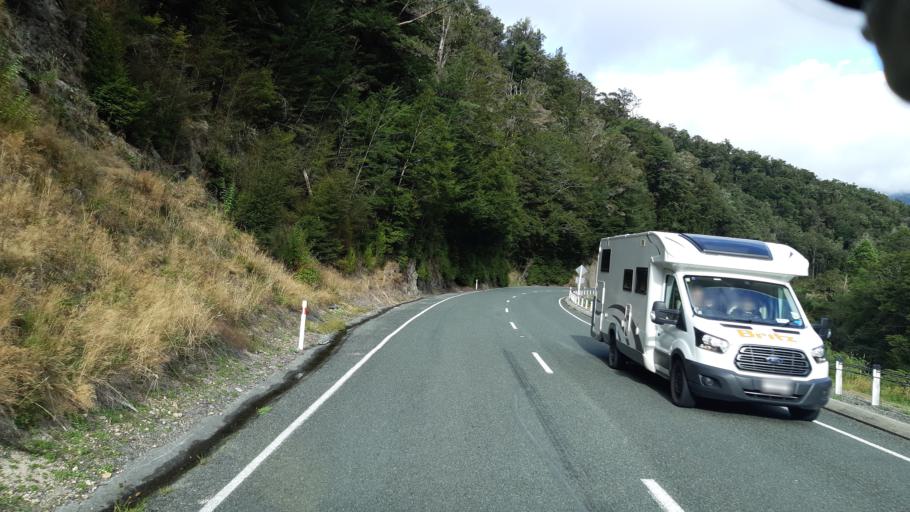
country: NZ
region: West Coast
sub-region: Buller District
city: Westport
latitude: -41.9882
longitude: 172.2166
